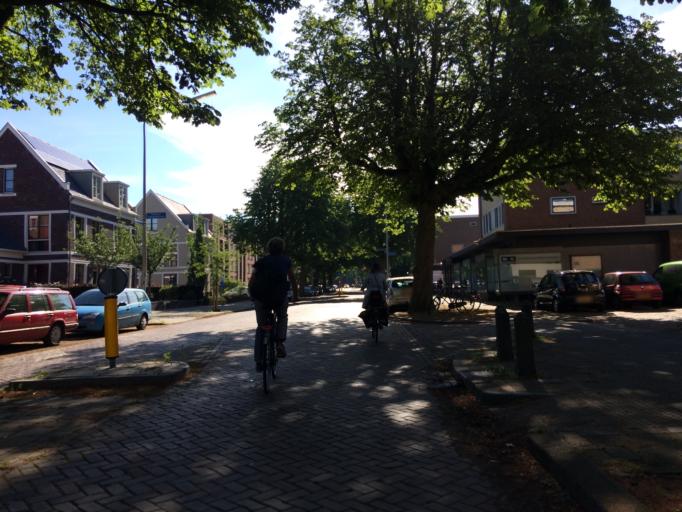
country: NL
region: Gelderland
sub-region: Gemeente Nijmegen
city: Nijmegen
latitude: 51.8343
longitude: 5.8666
